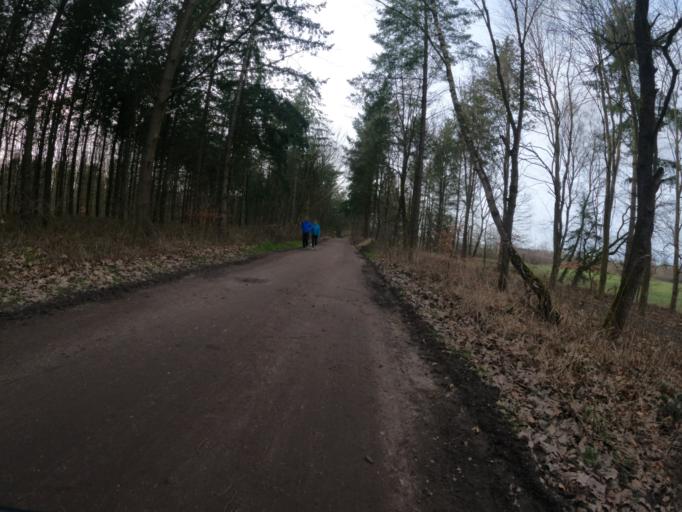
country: DE
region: Schleswig-Holstein
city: Appen
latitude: 53.6123
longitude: 9.7554
